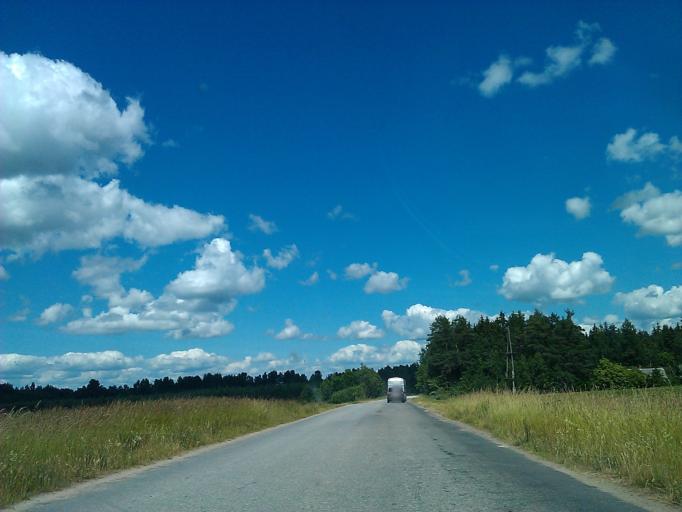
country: LV
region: Vilanu
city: Vilani
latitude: 56.5814
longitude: 26.9413
